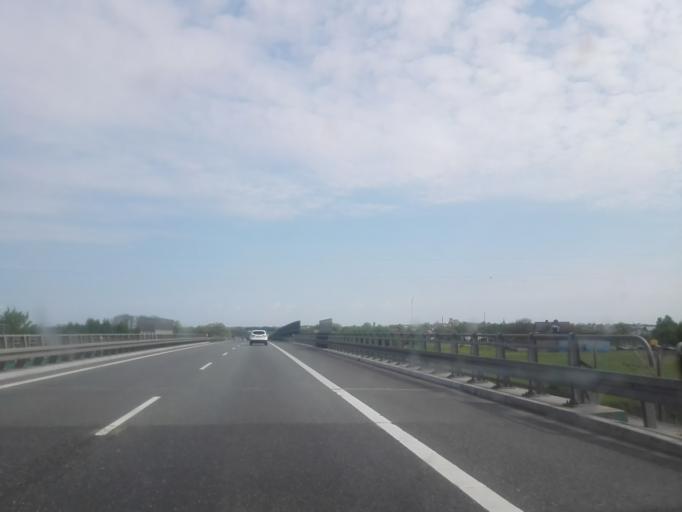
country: PL
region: Masovian Voivodeship
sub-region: Powiat zyrardowski
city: Mszczonow
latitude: 51.9668
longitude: 20.5013
